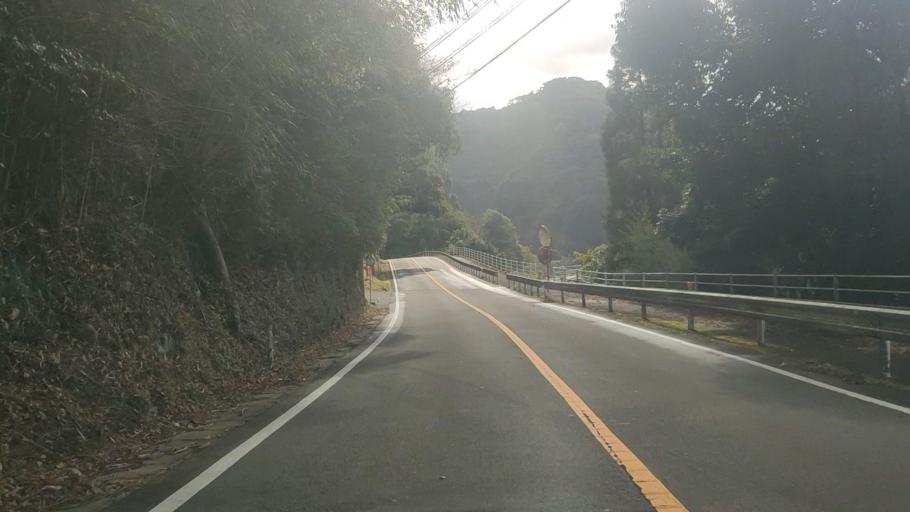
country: JP
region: Kumamoto
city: Hitoyoshi
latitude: 32.2903
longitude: 130.8450
